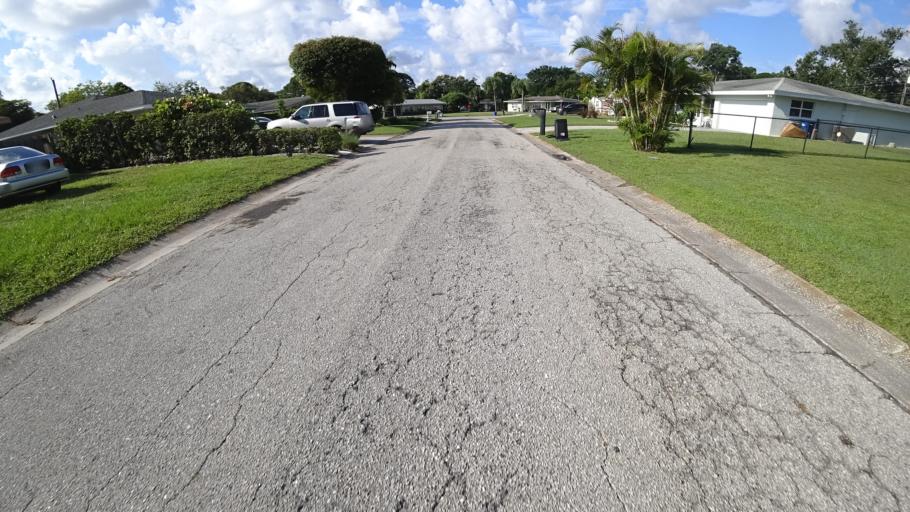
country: US
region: Florida
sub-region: Manatee County
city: South Bradenton
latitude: 27.4709
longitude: -82.5908
